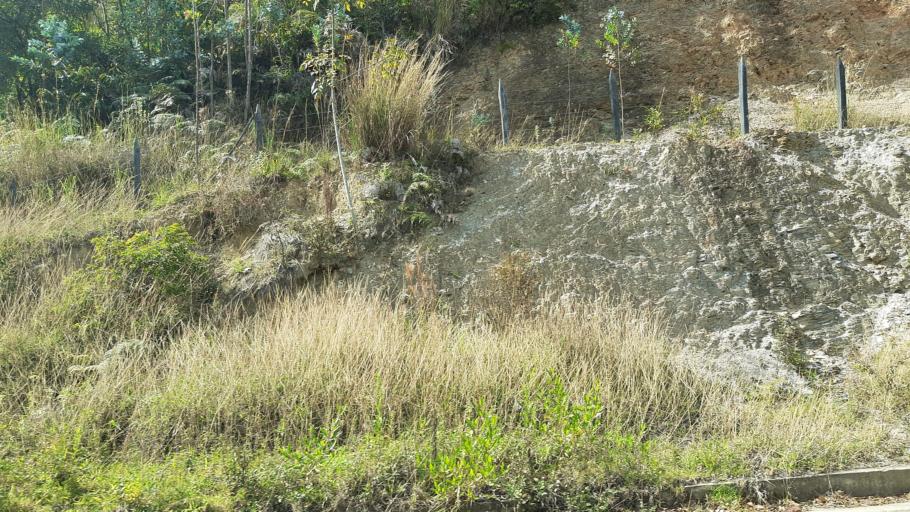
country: CO
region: Boyaca
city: Santa Sofia
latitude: 5.7601
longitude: -73.6034
